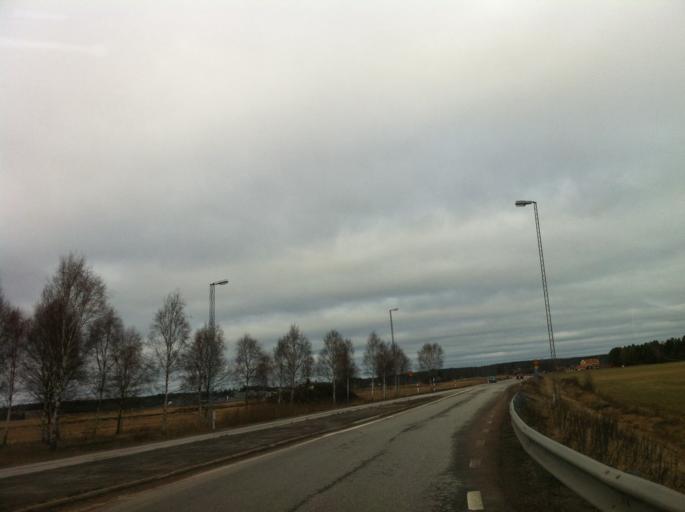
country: SE
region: Kalmar
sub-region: Vimmerby Kommun
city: Vimmerby
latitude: 57.6511
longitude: 15.8340
